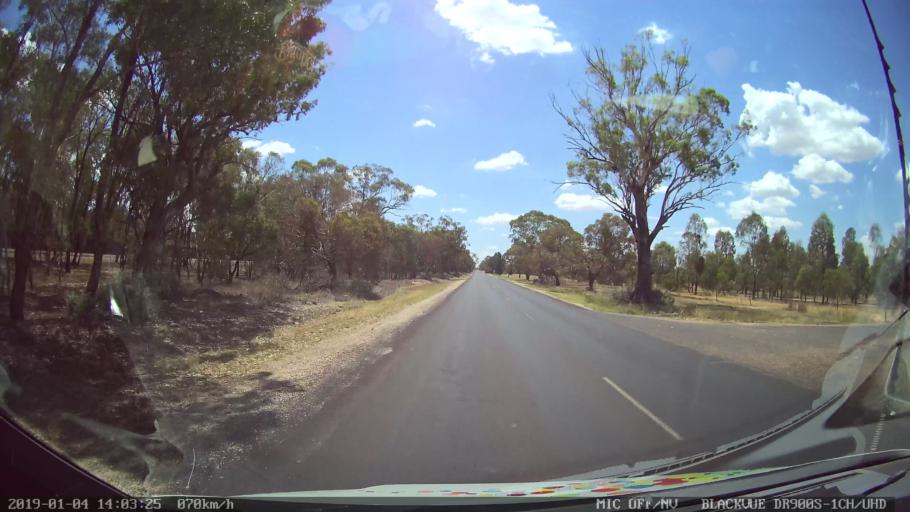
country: AU
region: New South Wales
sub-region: Dubbo Municipality
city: Dubbo
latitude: -32.2776
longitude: 148.5915
